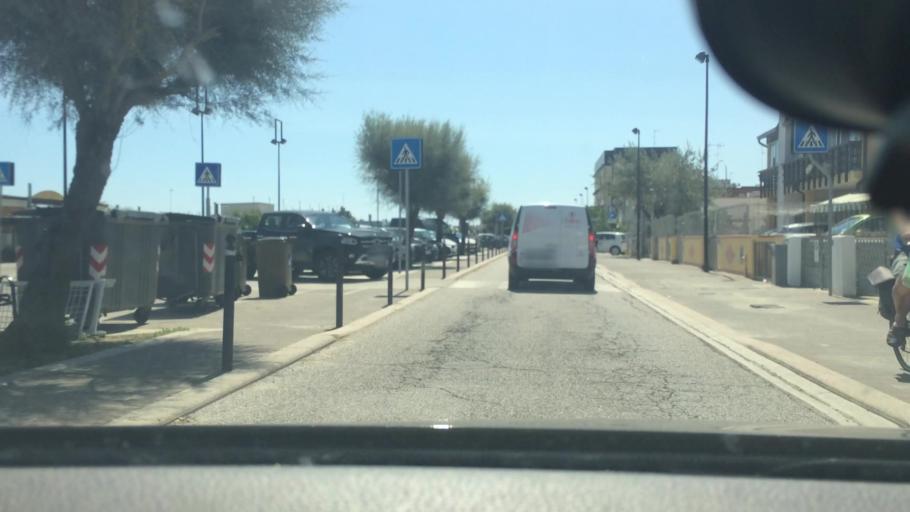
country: IT
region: Emilia-Romagna
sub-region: Provincia di Ferrara
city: Porto Garibaldi
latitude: 44.6846
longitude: 12.2405
